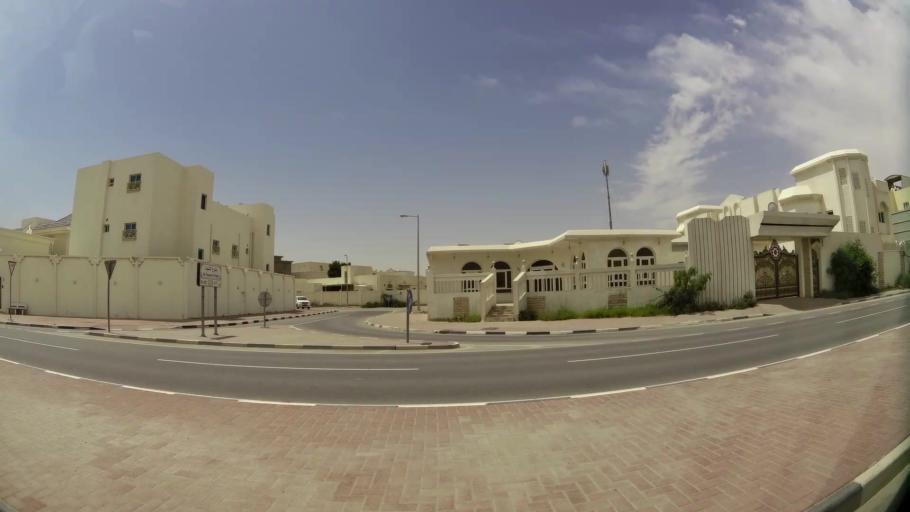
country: QA
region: Baladiyat ar Rayyan
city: Ar Rayyan
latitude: 25.2883
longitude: 51.4170
